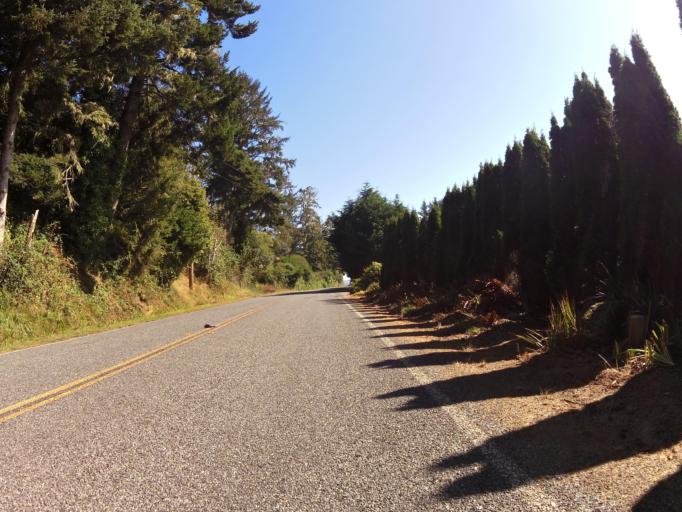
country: US
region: Oregon
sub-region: Curry County
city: Harbor
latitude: 41.9473
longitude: -124.1938
